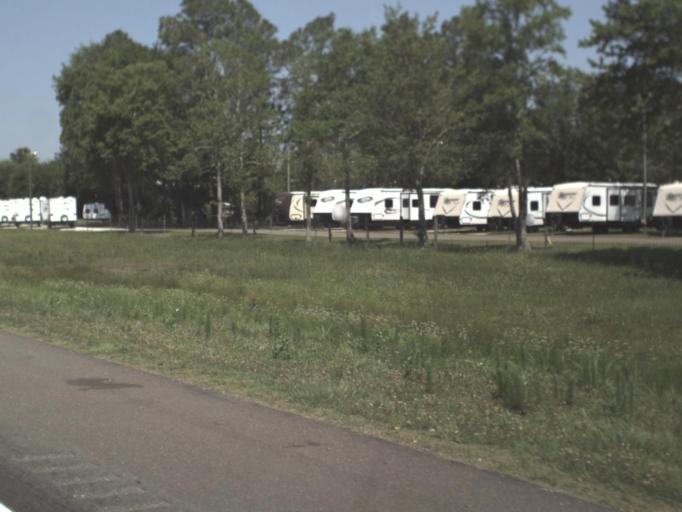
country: US
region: Florida
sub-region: Duval County
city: Baldwin
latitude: 30.3104
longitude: -81.8339
